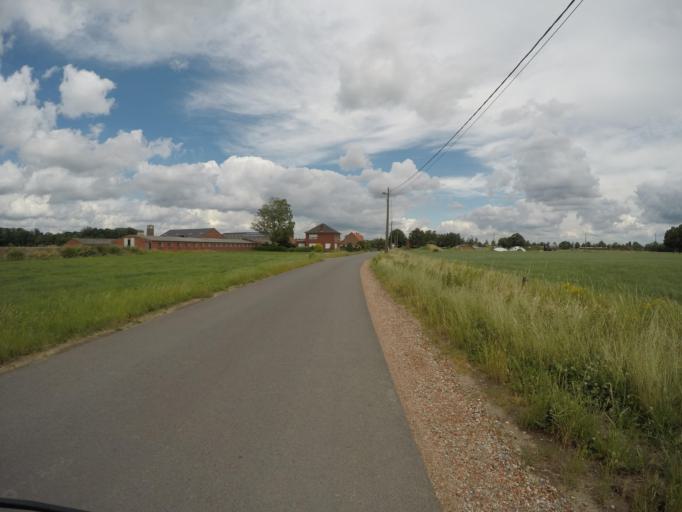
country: BE
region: Flanders
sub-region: Provincie Antwerpen
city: Rijkevorsel
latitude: 51.3690
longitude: 4.7486
